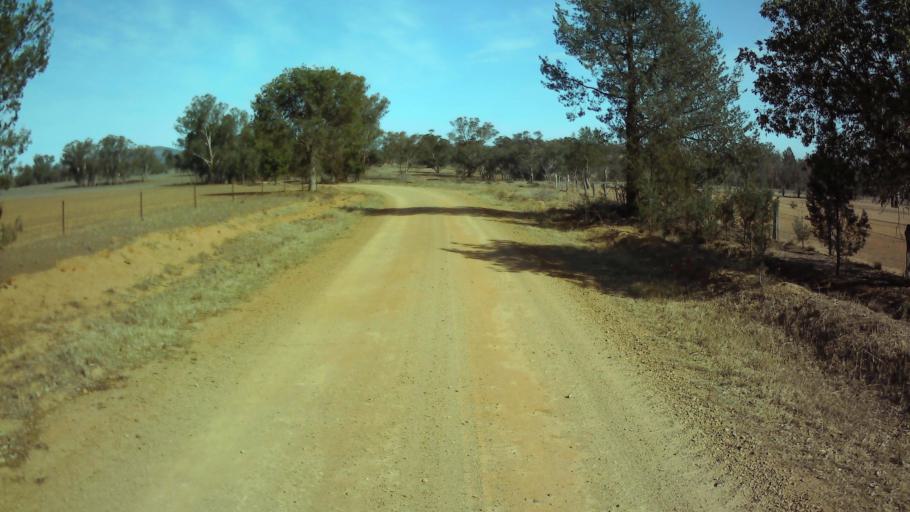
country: AU
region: New South Wales
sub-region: Weddin
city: Grenfell
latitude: -33.7606
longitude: 148.0333
